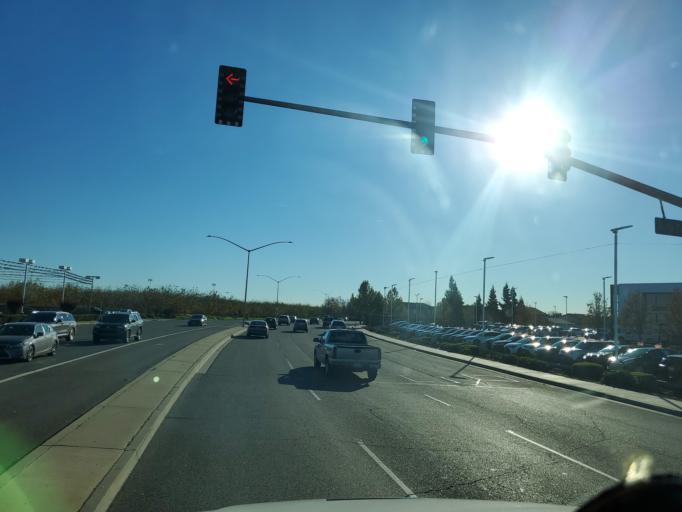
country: US
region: California
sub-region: San Joaquin County
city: Morada
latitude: 38.0174
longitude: -121.2706
